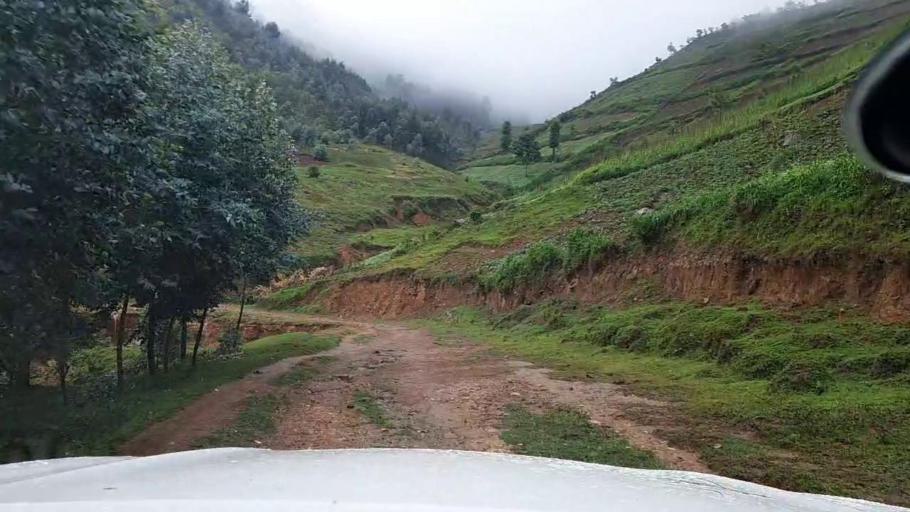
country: RW
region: Western Province
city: Kibuye
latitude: -2.1459
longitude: 29.4581
